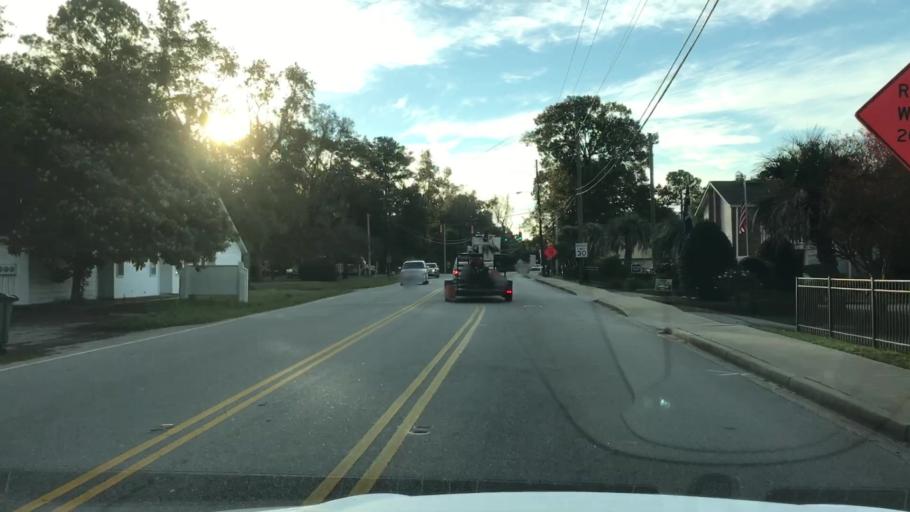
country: US
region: South Carolina
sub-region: Charleston County
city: North Charleston
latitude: 32.8112
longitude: -80.0113
